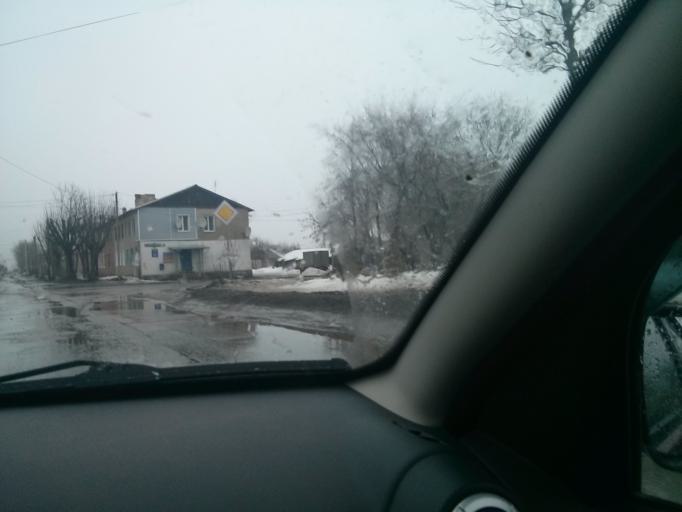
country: RU
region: Vladimir
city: Murom
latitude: 55.5840
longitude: 42.0366
